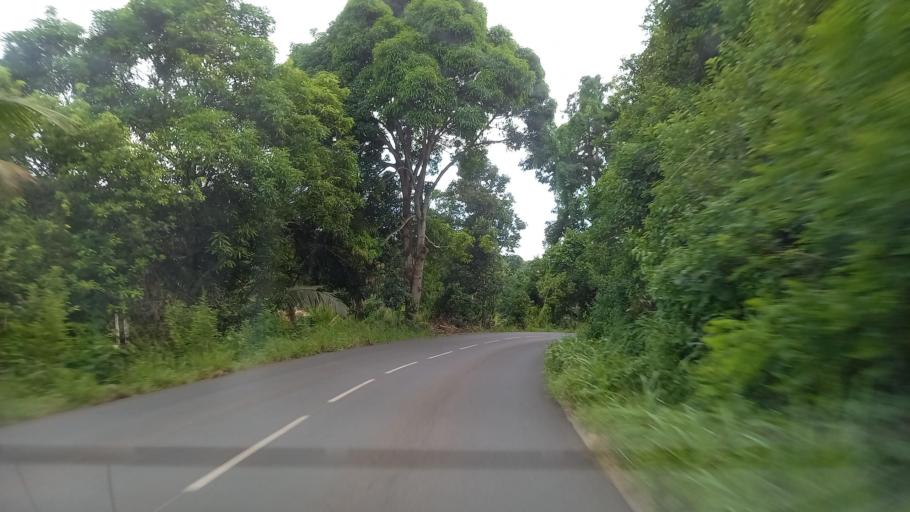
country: YT
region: M'Tsangamouji
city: M'Tsangamouji
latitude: -12.7565
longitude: 45.1122
